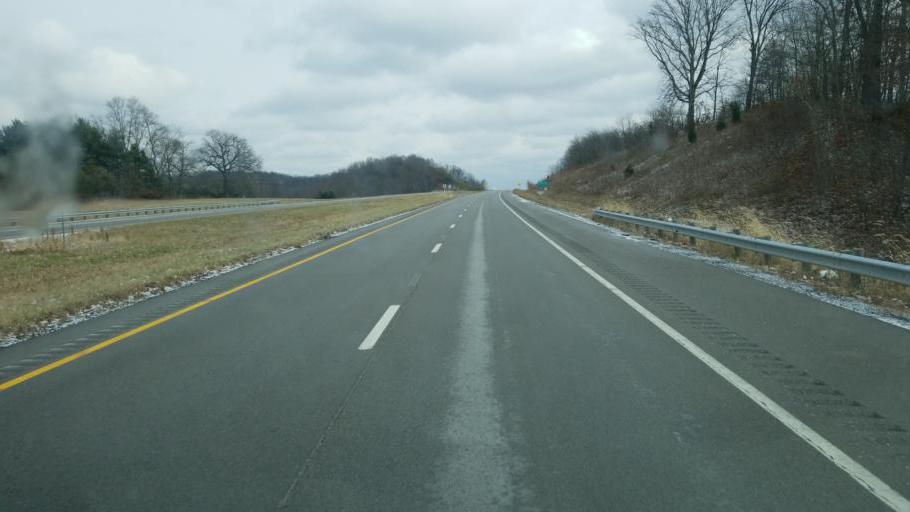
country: US
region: Ohio
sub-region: Muskingum County
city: Frazeysburg
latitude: 40.1252
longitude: -82.1346
